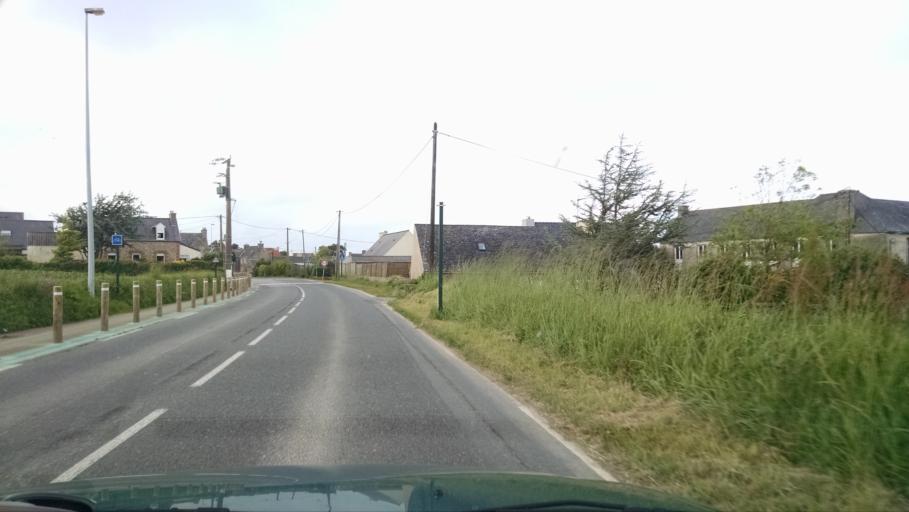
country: FR
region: Brittany
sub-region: Departement du Finistere
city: Saint-Pol-de-Leon
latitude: 48.6974
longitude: -3.9870
